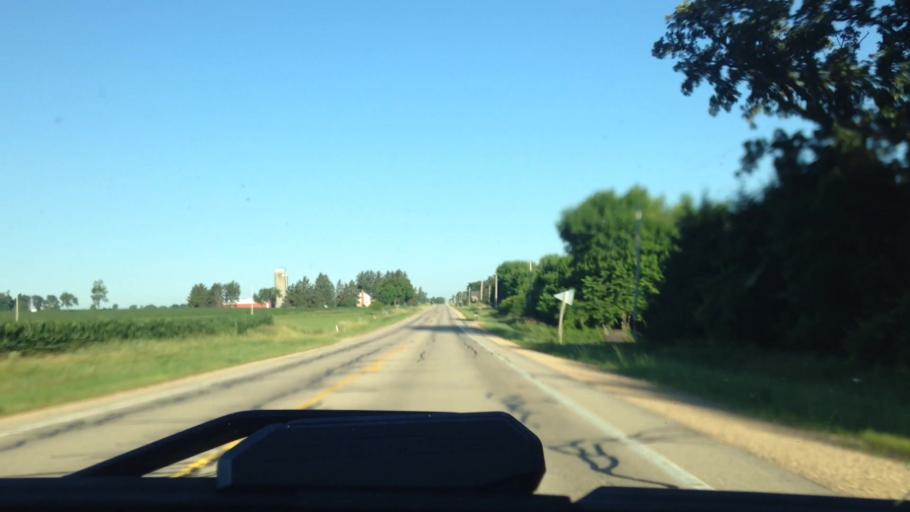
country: US
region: Wisconsin
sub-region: Columbia County
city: Fall River
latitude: 43.3415
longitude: -89.0774
